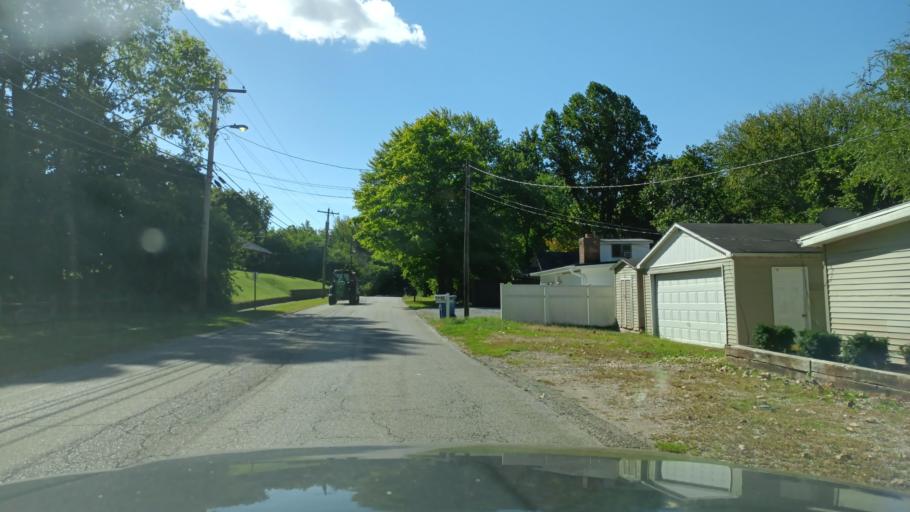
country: US
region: Indiana
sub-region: Fountain County
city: Covington
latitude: 40.1357
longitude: -87.3863
